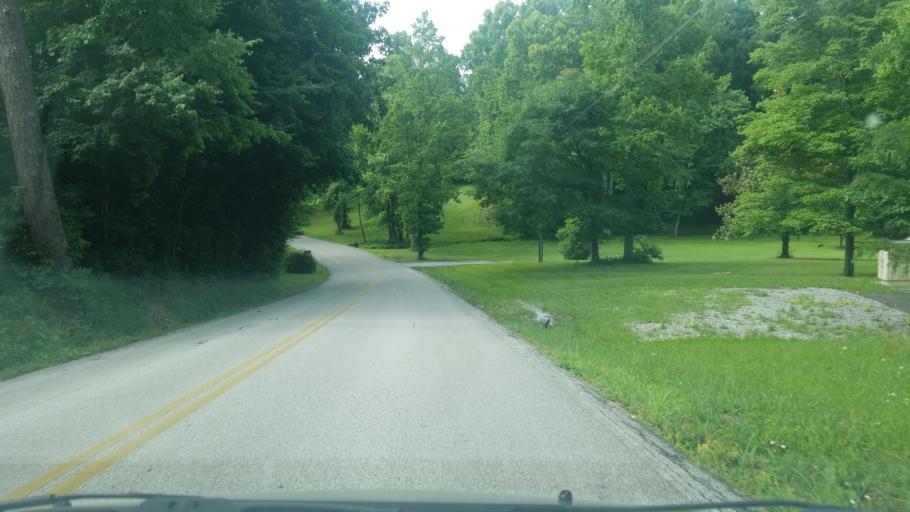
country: US
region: Tennessee
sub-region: Hamilton County
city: Collegedale
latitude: 35.0251
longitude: -85.0605
